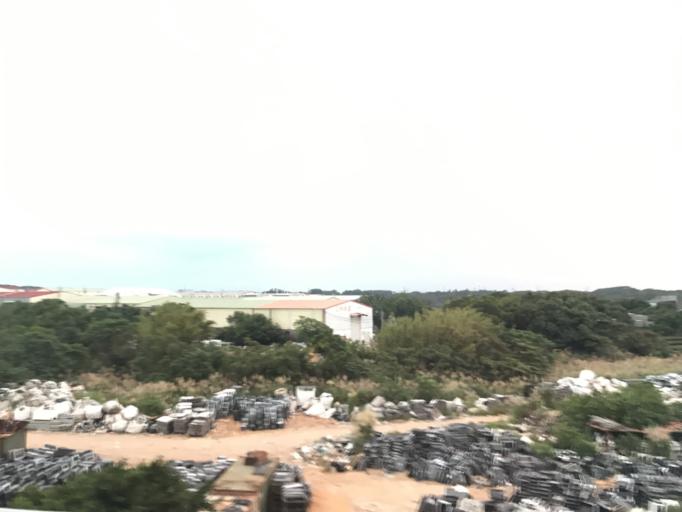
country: TW
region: Taiwan
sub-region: Taoyuan
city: Taoyuan
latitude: 25.0650
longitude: 121.3439
